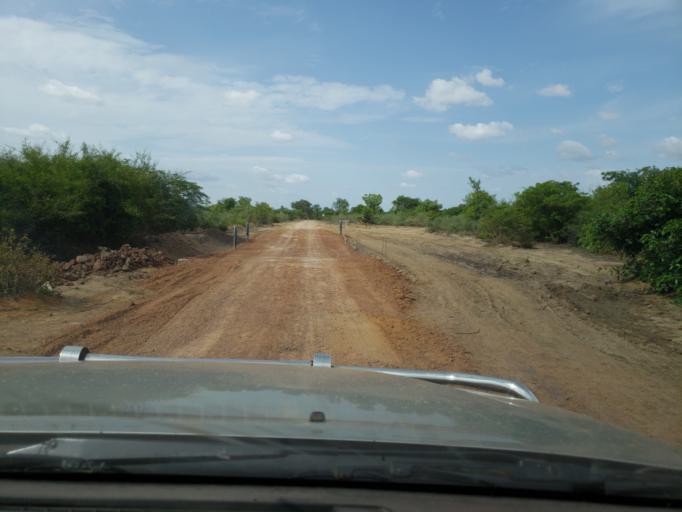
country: ML
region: Segou
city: Bla
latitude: 12.7636
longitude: -5.6225
